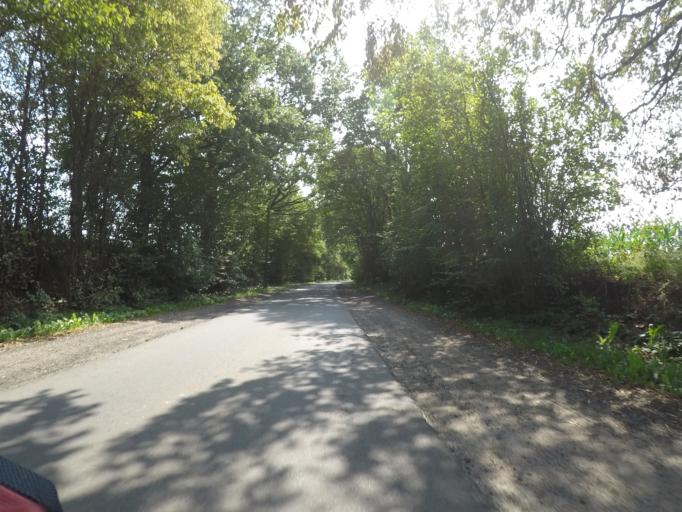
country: DE
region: Schleswig-Holstein
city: Kisdorf
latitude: 53.8034
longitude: 10.0137
